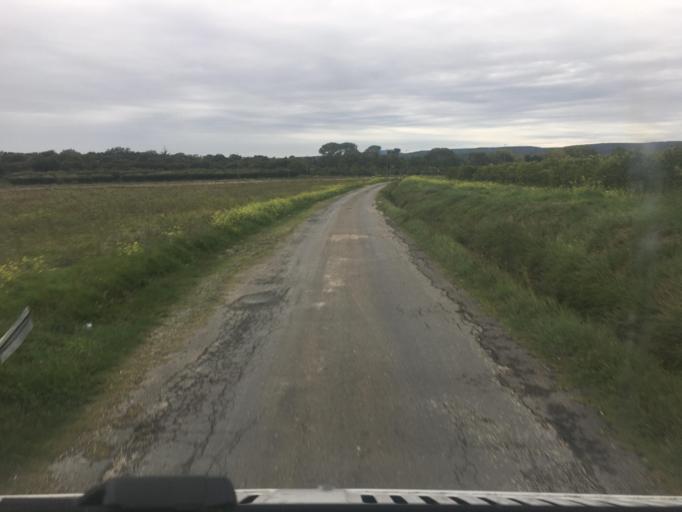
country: FR
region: Languedoc-Roussillon
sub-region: Departement du Gard
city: Uzes
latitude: 44.0222
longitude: 4.4048
